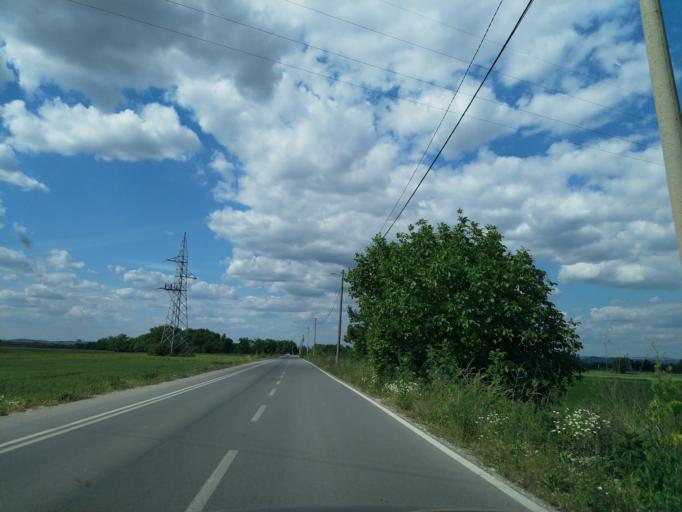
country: RS
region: Central Serbia
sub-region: Pomoravski Okrug
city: Jagodina
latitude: 43.9543
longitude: 21.2909
